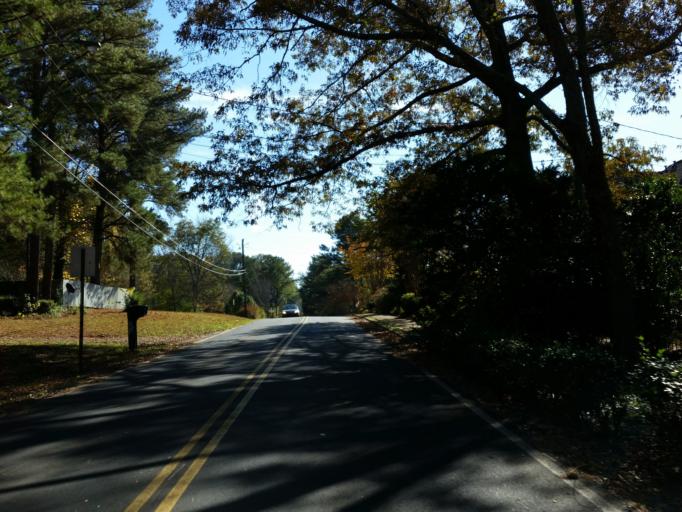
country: US
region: Georgia
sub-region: Cherokee County
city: Woodstock
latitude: 34.0307
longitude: -84.4858
